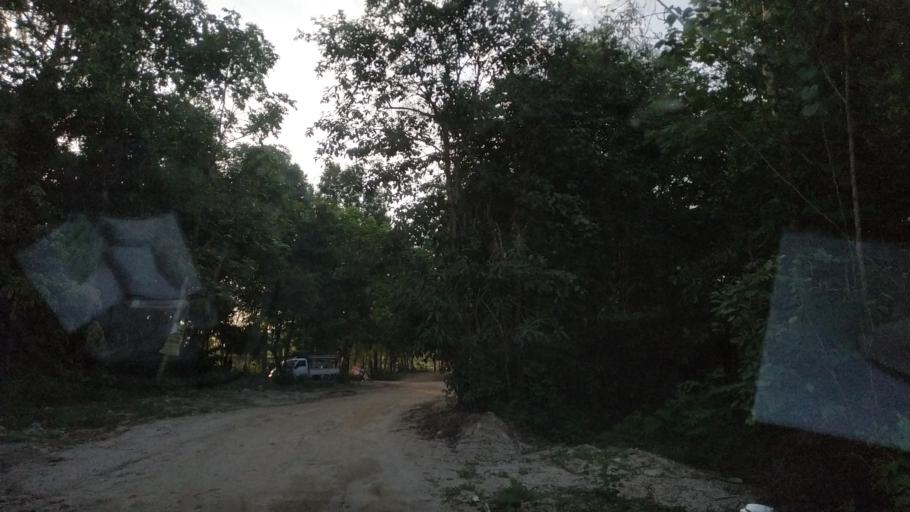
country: MM
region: Mon
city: Kyaikto
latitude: 17.4358
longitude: 97.0403
